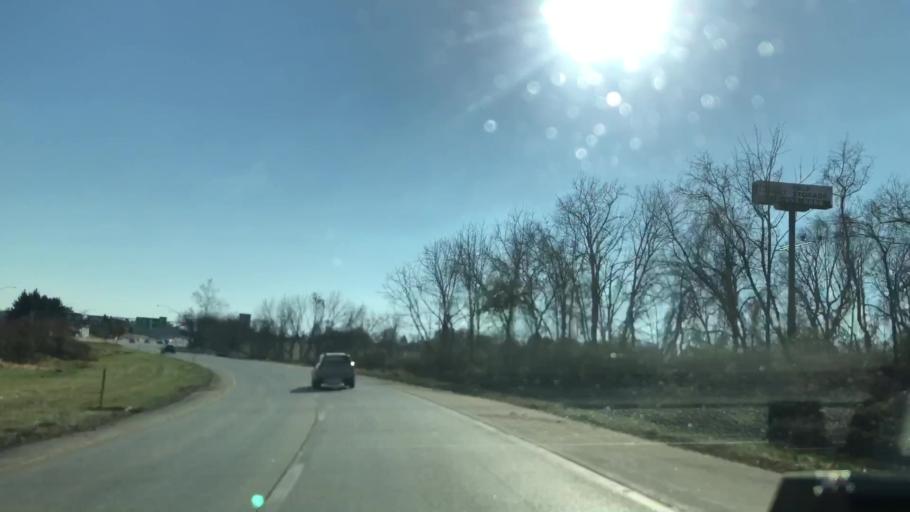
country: US
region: Pennsylvania
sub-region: Lehigh County
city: Wescosville
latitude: 40.5770
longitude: -75.5512
